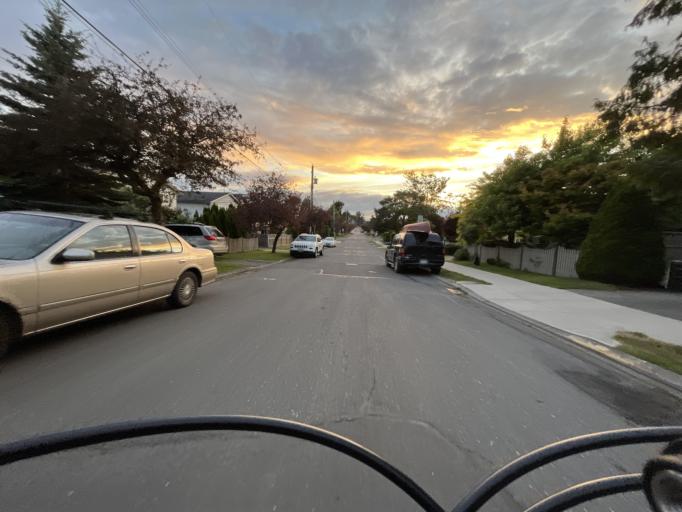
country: CA
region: British Columbia
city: Victoria
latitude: 48.4255
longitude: -123.4090
